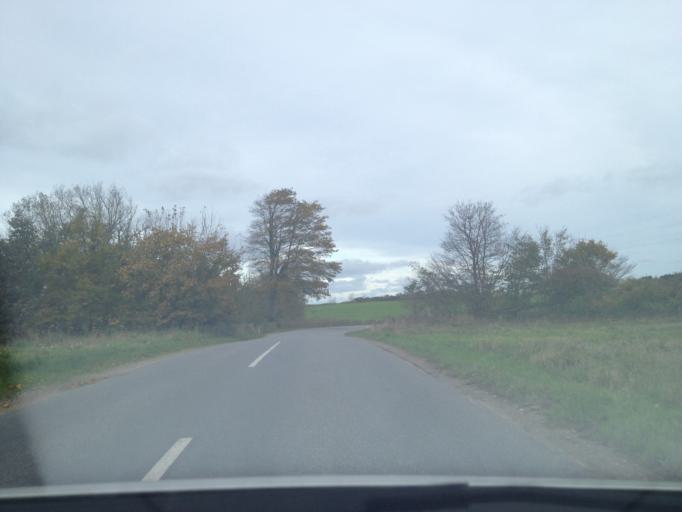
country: DK
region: Zealand
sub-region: Odsherred Kommune
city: Hojby
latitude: 55.9266
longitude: 11.5978
